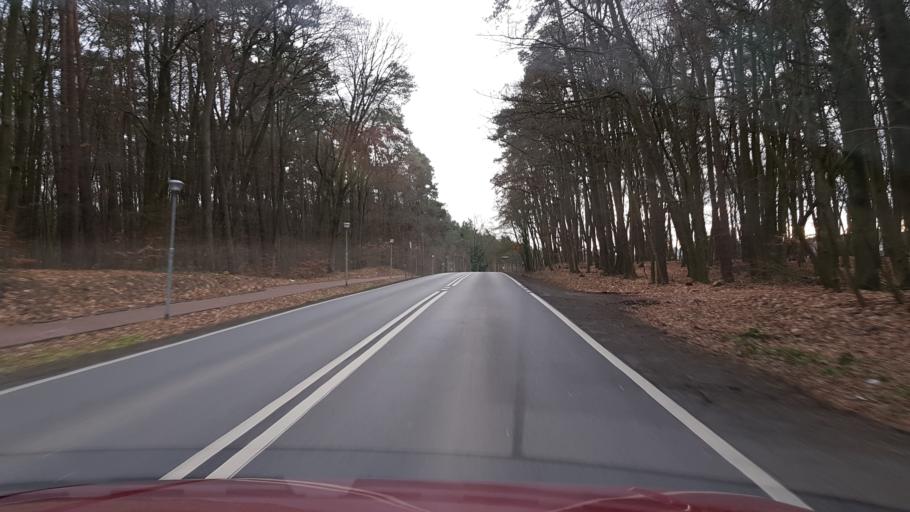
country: PL
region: West Pomeranian Voivodeship
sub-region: Szczecin
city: Szczecin
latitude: 53.4812
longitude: 14.4842
